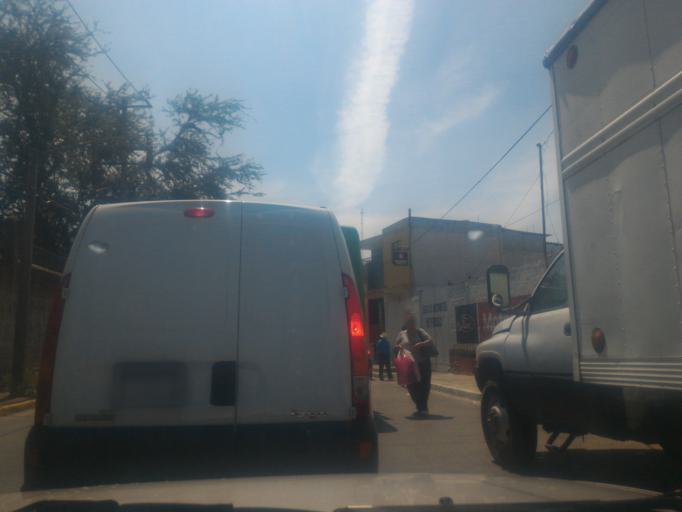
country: MX
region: Jalisco
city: Las Pintas de Arriba
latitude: 20.6232
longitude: -103.3475
